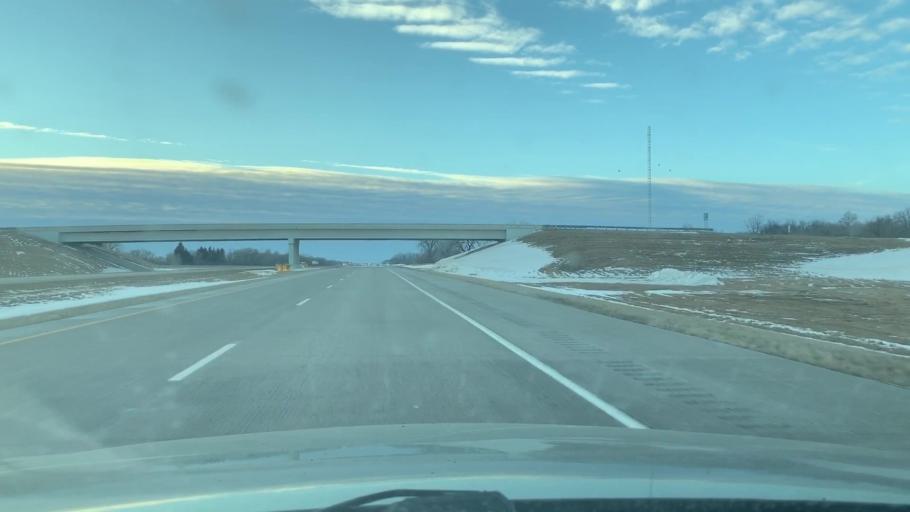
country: US
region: North Dakota
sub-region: Cass County
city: Casselton
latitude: 46.8766
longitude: -97.4282
